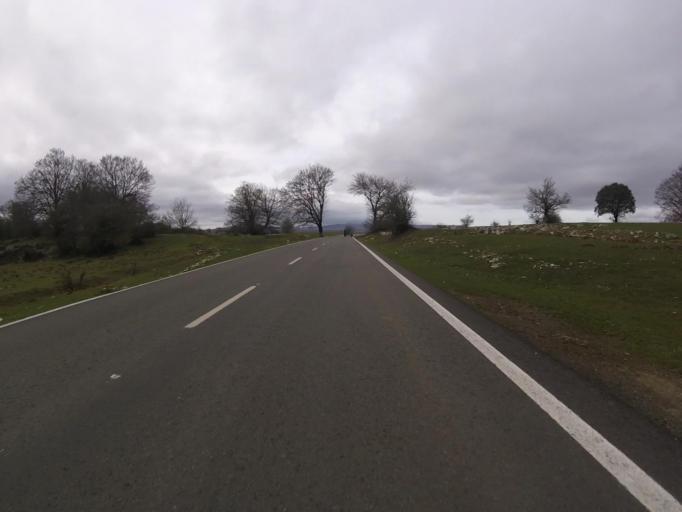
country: ES
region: Navarre
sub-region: Provincia de Navarra
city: Eulate
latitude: 42.8011
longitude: -2.1469
